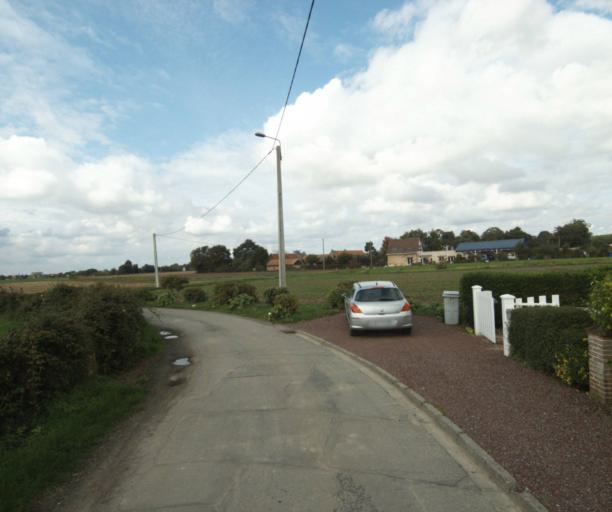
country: FR
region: Nord-Pas-de-Calais
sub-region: Departement du Nord
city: Ennetieres-en-Weppes
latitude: 50.6500
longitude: 2.9304
